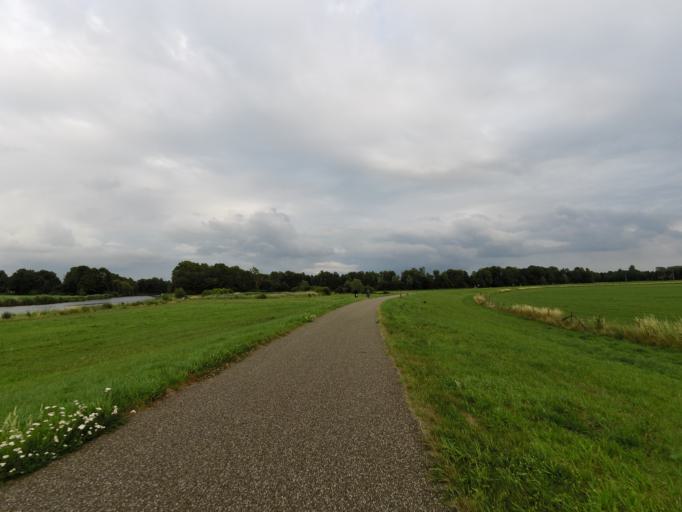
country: NL
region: Gelderland
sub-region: Gemeente Doetinchem
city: Doetinchem
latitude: 51.9742
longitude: 6.2503
